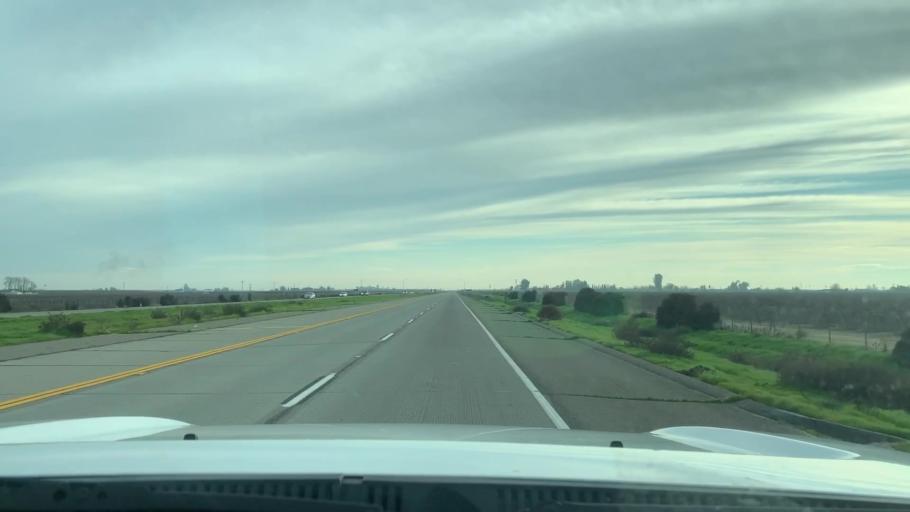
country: US
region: California
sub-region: Fresno County
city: Caruthers
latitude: 36.5679
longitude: -119.7863
